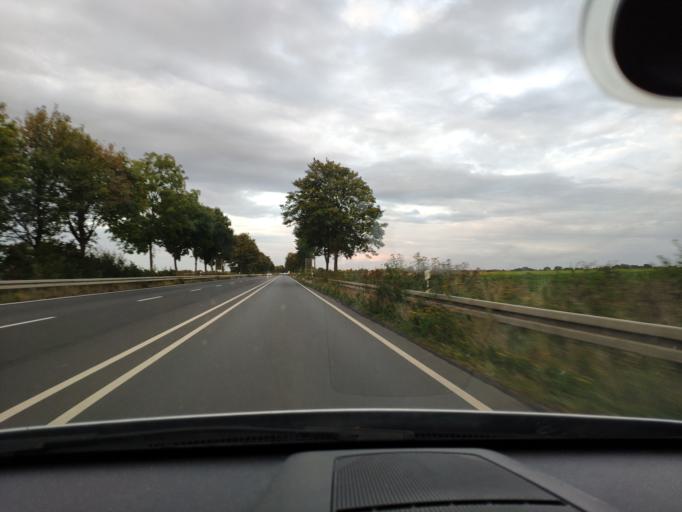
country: DE
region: North Rhine-Westphalia
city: Geilenkirchen
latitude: 50.9532
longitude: 6.1384
